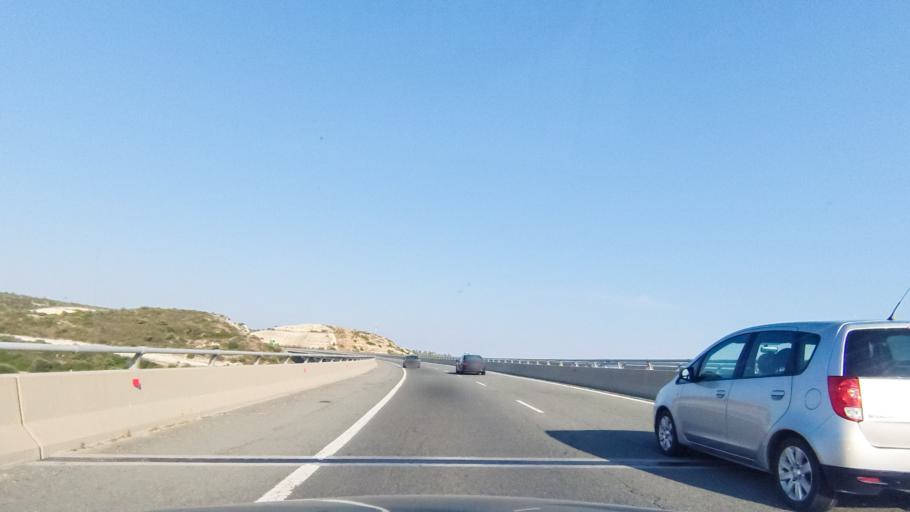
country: CY
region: Limassol
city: Sotira
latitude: 34.6792
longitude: 32.7936
